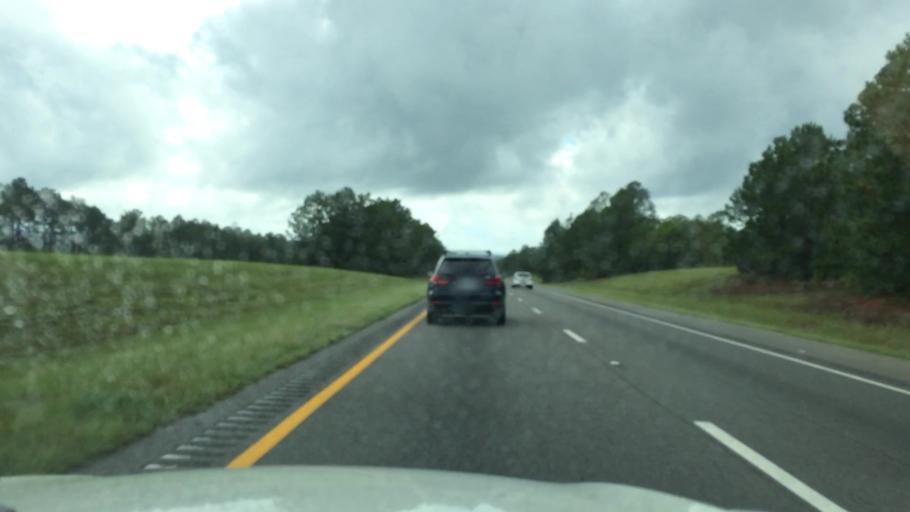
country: US
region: South Carolina
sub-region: Kershaw County
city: Lugoff
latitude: 34.1647
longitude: -80.7197
